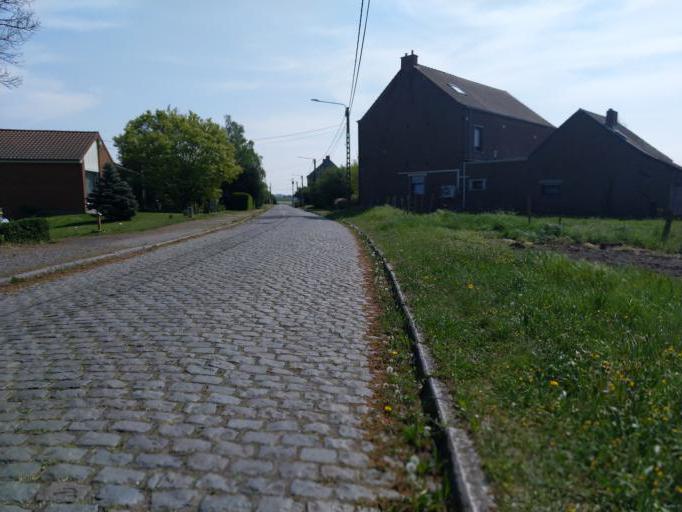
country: BE
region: Wallonia
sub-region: Province du Hainaut
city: Mons
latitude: 50.4557
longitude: 4.0345
